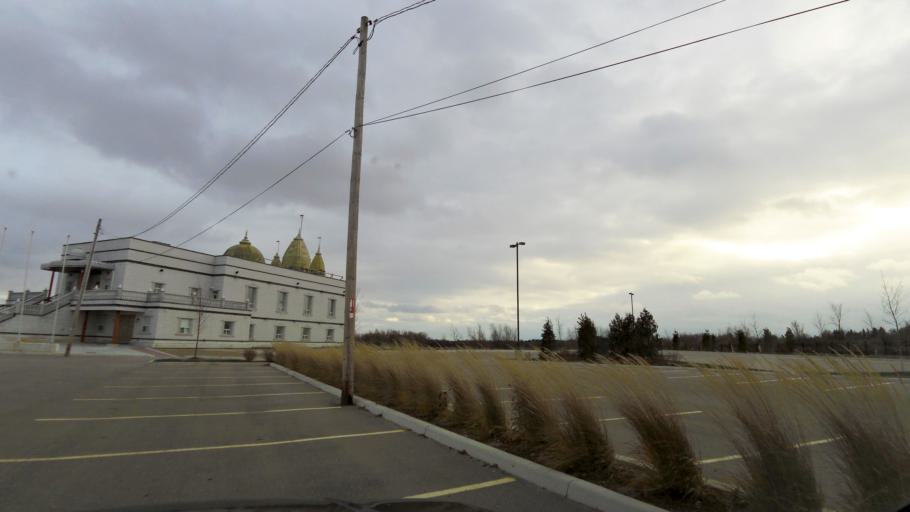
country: CA
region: Ontario
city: Brampton
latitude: 43.8269
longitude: -79.7183
